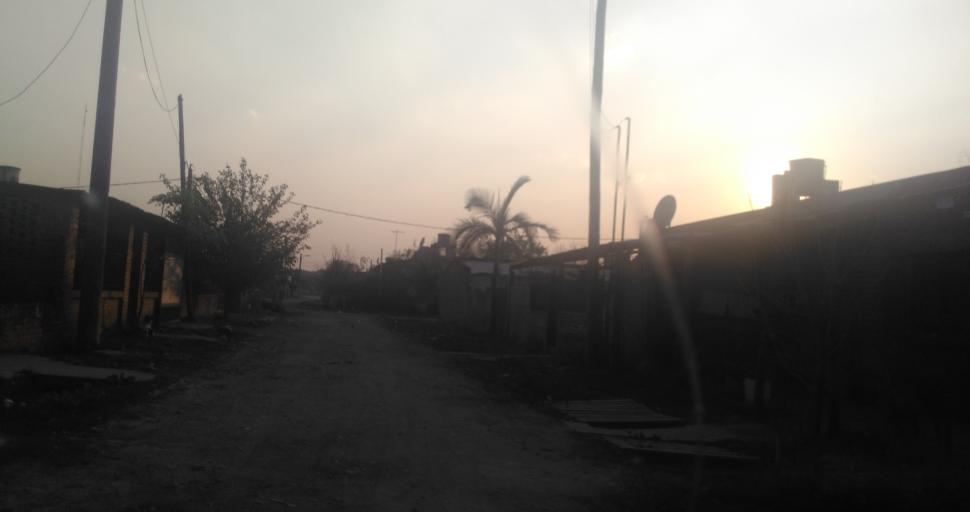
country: AR
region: Chaco
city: Resistencia
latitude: -27.4642
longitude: -59.0190
